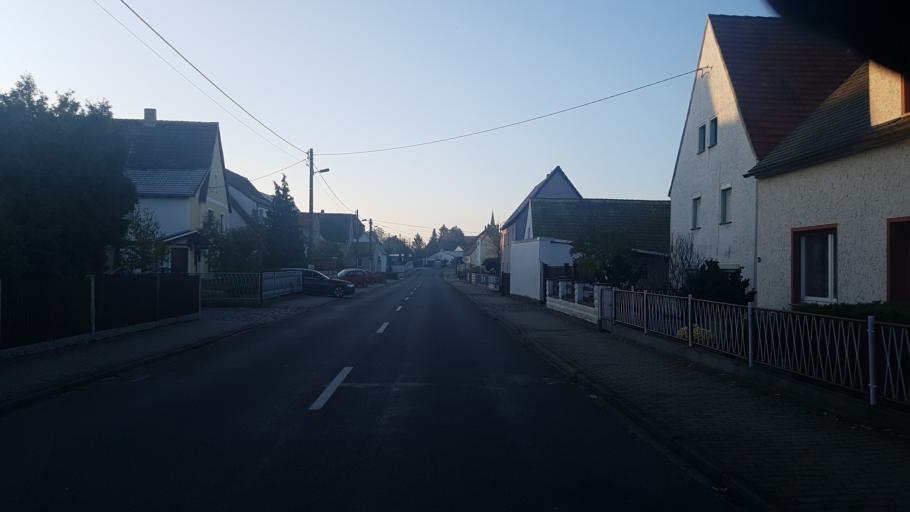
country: DE
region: Saxony
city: Schildau
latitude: 51.4491
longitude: 12.9703
